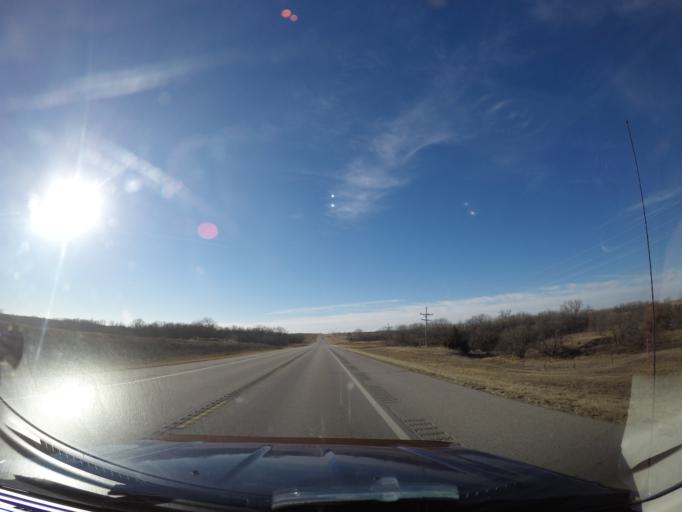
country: US
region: Kansas
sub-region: Marion County
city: Hillsboro
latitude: 38.3625
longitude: -97.3195
